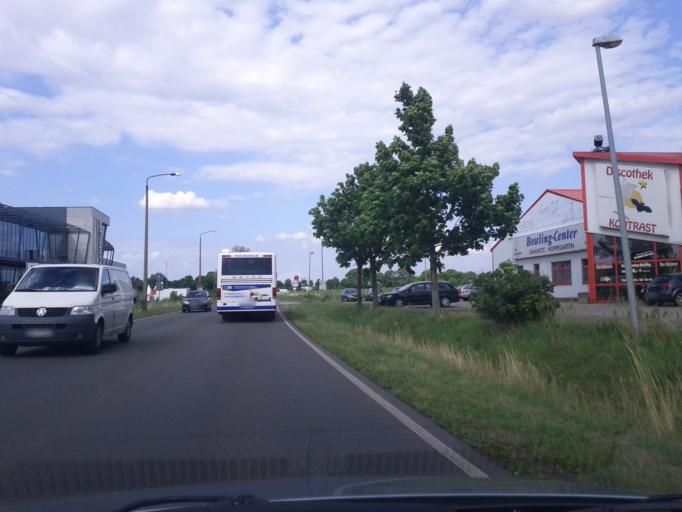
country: DE
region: Brandenburg
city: Hoppegarten
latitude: 52.5078
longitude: 13.6482
